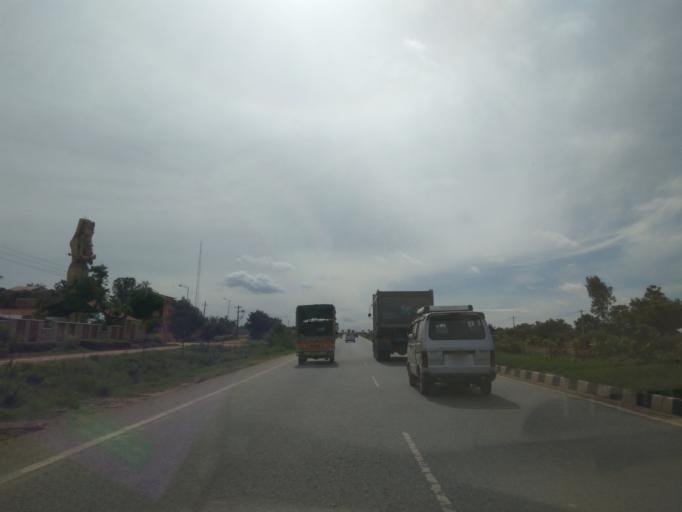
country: IN
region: Karnataka
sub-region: Bangalore Rural
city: Dasarahalli
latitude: 13.1326
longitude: 77.9518
